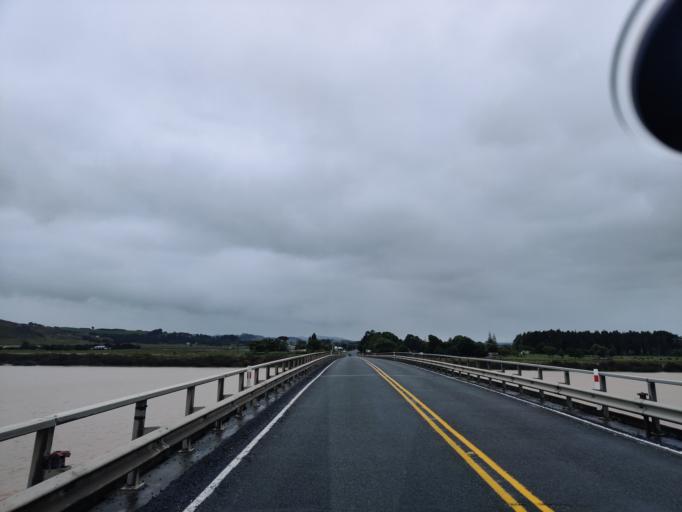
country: NZ
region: Northland
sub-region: Kaipara District
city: Dargaville
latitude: -35.9390
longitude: 173.8839
